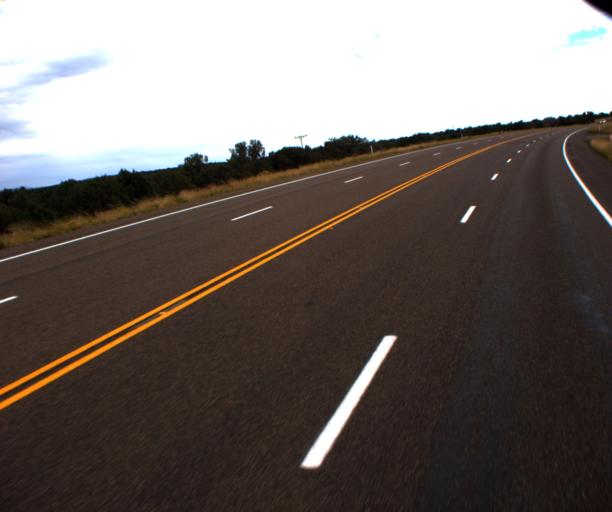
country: US
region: Arizona
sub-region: Navajo County
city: White Mountain Lake
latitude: 34.3707
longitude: -110.0511
